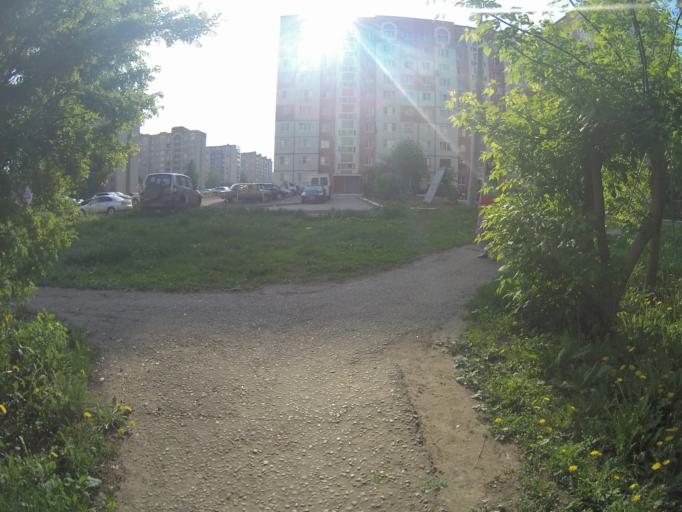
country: RU
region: Vladimir
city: Kommunar
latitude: 56.1705
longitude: 40.4521
